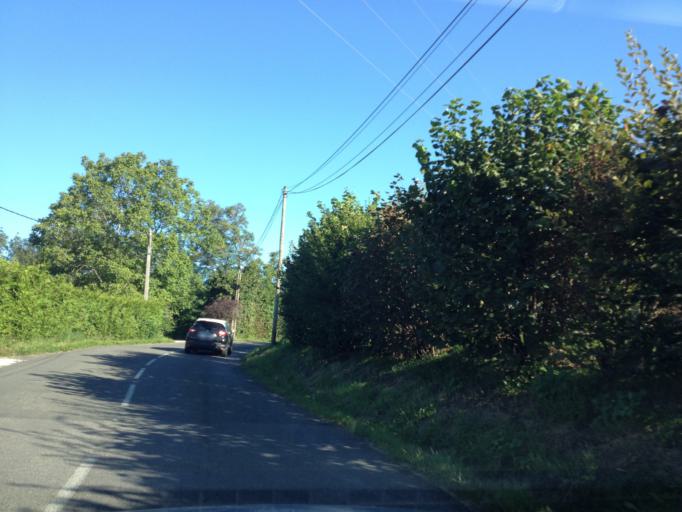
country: FR
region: Rhone-Alpes
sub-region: Departement de la Savoie
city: Mouxy
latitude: 45.7038
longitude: 5.9508
